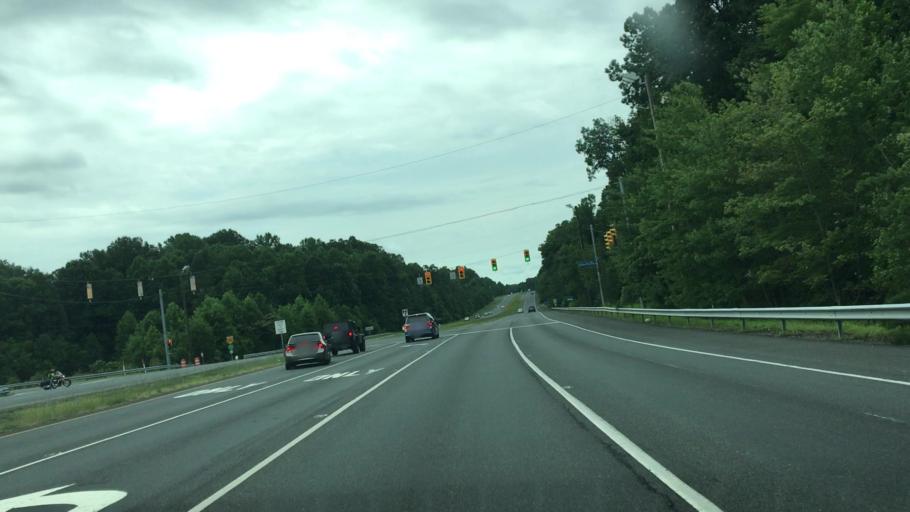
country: US
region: Virginia
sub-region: Prince William County
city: Buckhall
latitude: 38.7307
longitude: -77.4238
